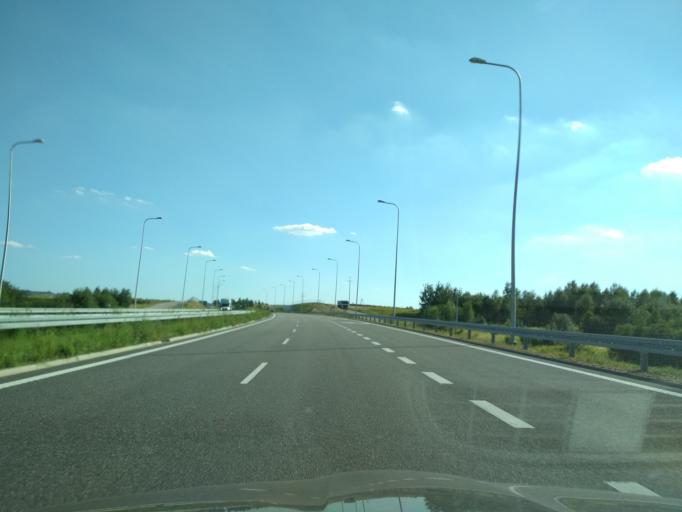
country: PL
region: Subcarpathian Voivodeship
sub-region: Rzeszow
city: Przybyszowka
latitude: 50.0633
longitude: 21.9253
